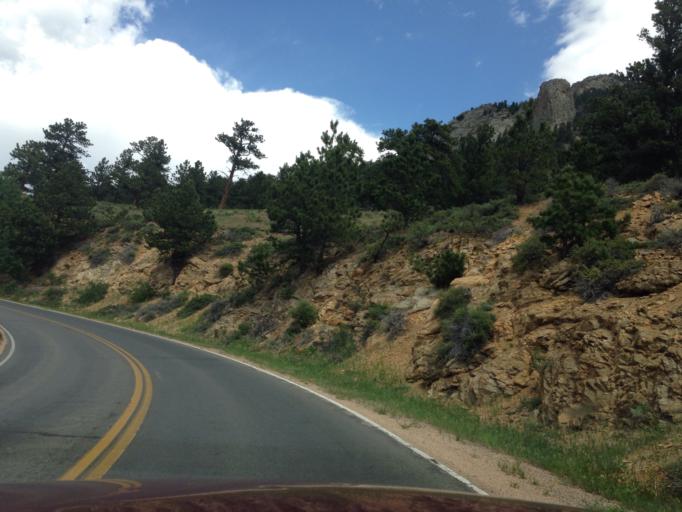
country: US
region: Colorado
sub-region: Larimer County
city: Estes Park
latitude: 40.3706
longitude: -105.5862
